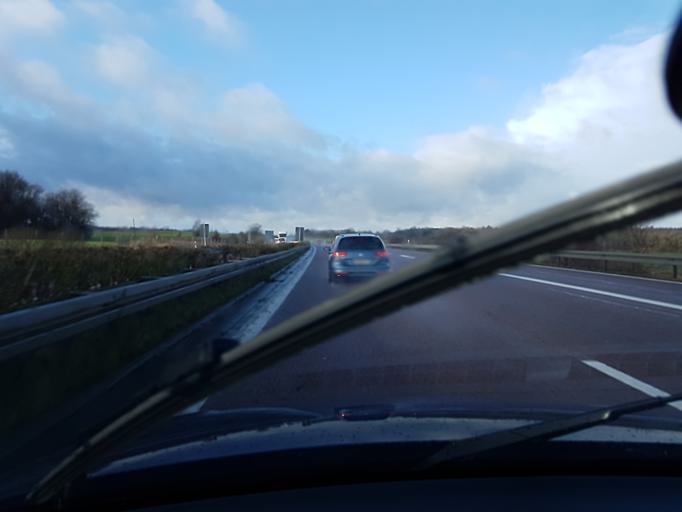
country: DE
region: Mecklenburg-Vorpommern
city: Tessin
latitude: 54.0324
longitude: 12.4048
